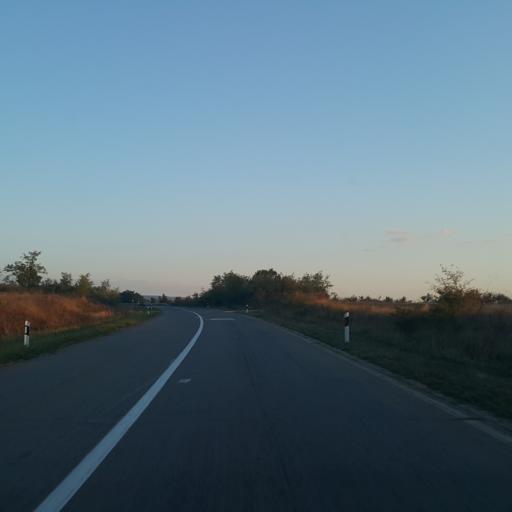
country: RS
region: Central Serbia
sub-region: Zajecarski Okrug
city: Zajecar
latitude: 44.0073
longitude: 22.3035
